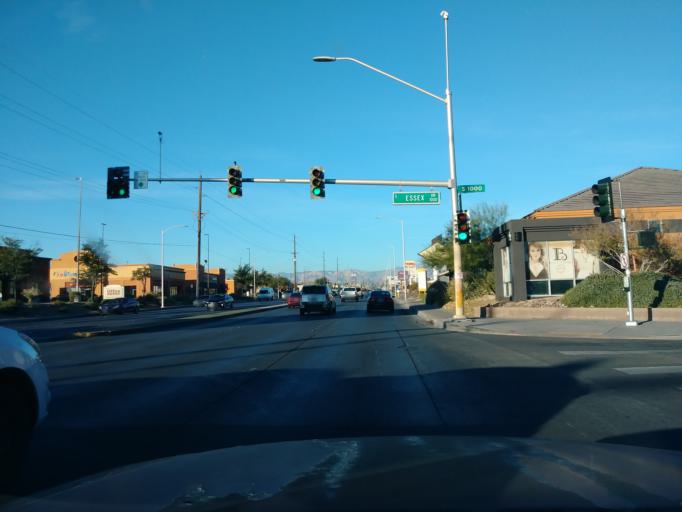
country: US
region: Nevada
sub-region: Clark County
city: Las Vegas
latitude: 36.1592
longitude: -115.2013
